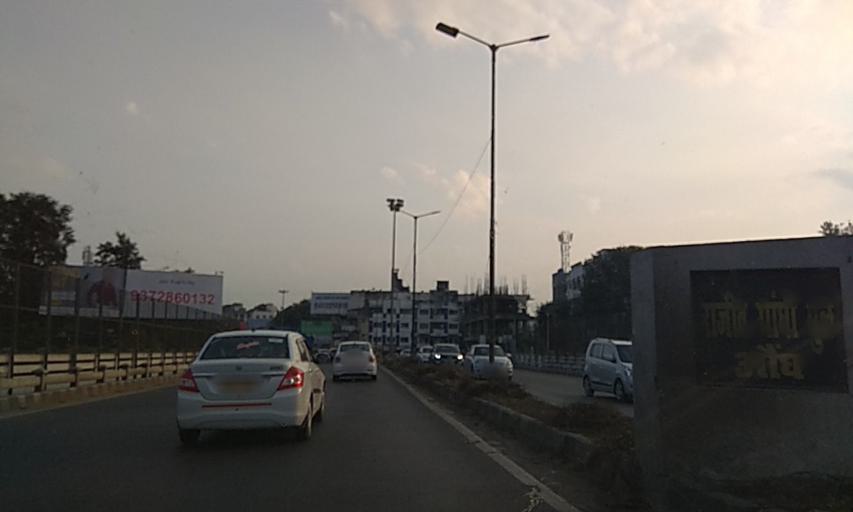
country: IN
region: Maharashtra
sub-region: Pune Division
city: Khadki
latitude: 18.5680
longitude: 73.8116
